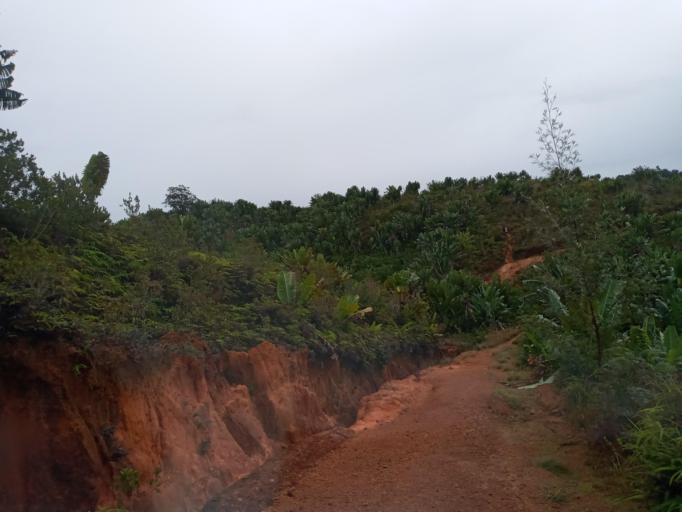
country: MG
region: Atsimo-Atsinanana
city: Vohipaho
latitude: -24.0000
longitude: 47.4044
